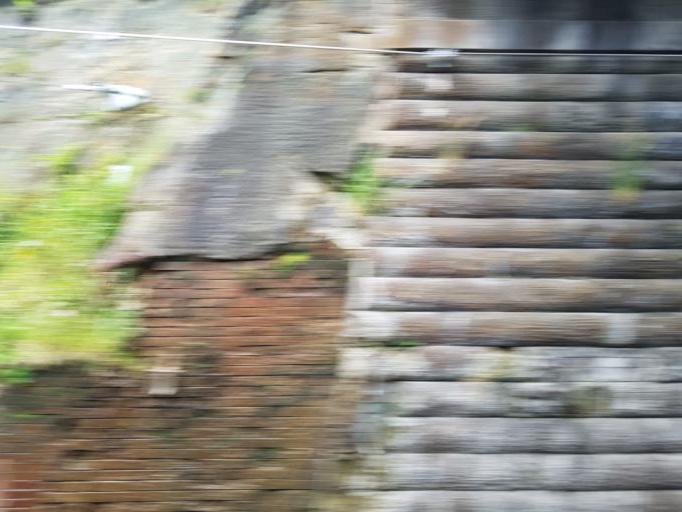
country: GB
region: Scotland
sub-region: East Dunbartonshire
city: Bishopbriggs
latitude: 55.8951
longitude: -4.2386
